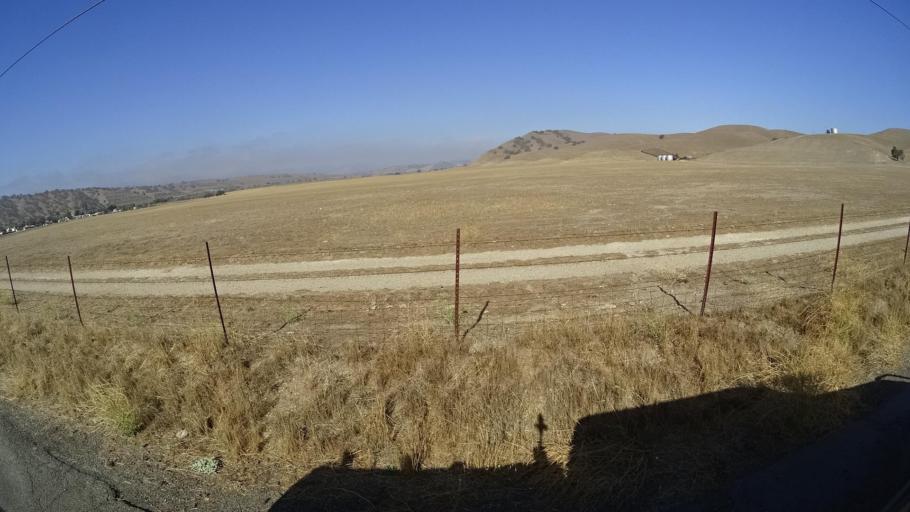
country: US
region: California
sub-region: San Luis Obispo County
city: San Miguel
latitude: 35.8678
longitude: -120.7949
